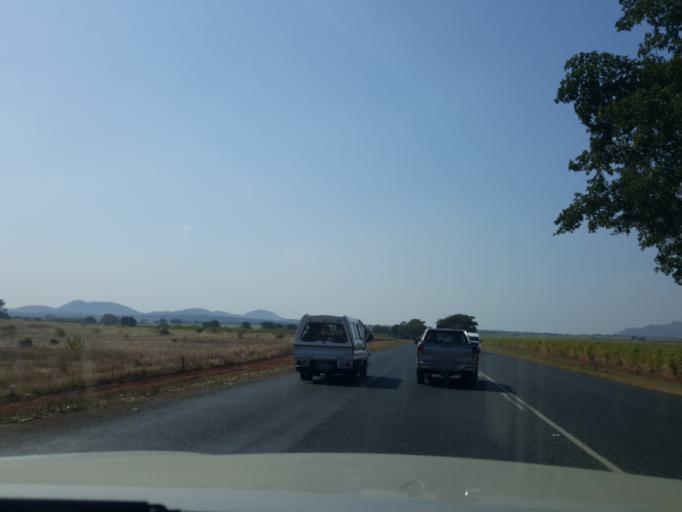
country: SZ
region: Hhohho
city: Ntfonjeni
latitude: -25.4924
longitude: 31.5245
